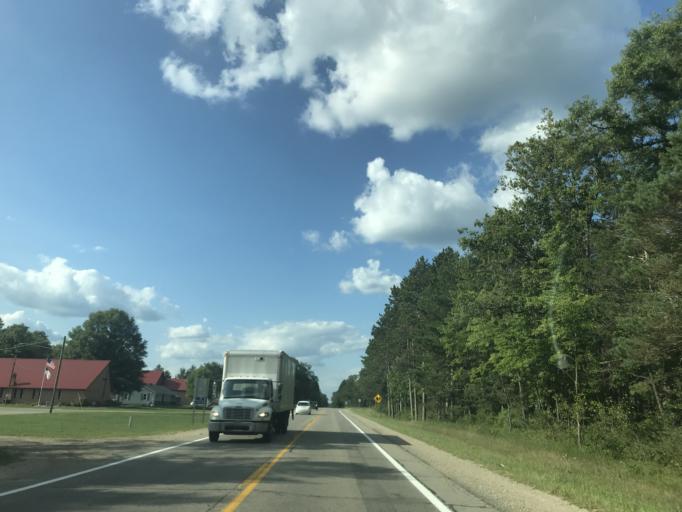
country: US
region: Michigan
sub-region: Newaygo County
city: White Cloud
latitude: 43.5234
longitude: -85.7718
